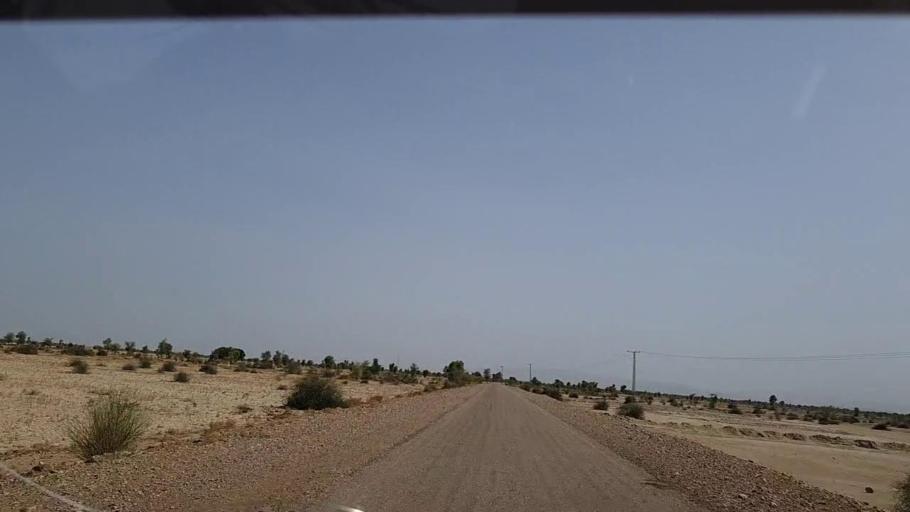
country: PK
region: Sindh
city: Johi
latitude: 26.6610
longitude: 67.5062
